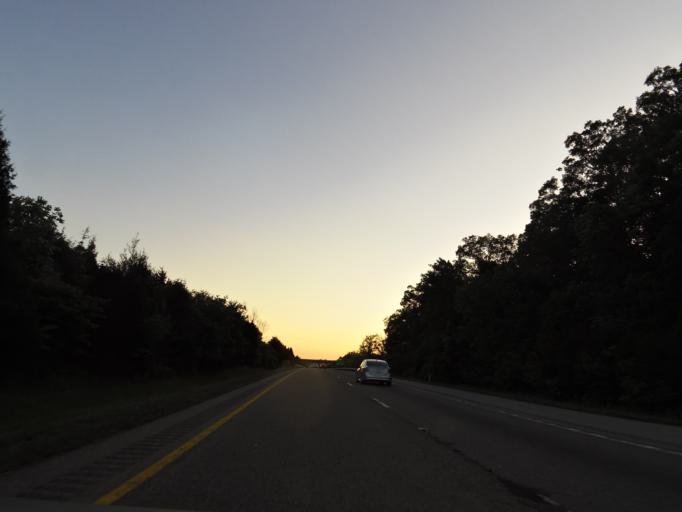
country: US
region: Tennessee
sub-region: Greene County
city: Mosheim
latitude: 36.2183
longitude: -83.0583
